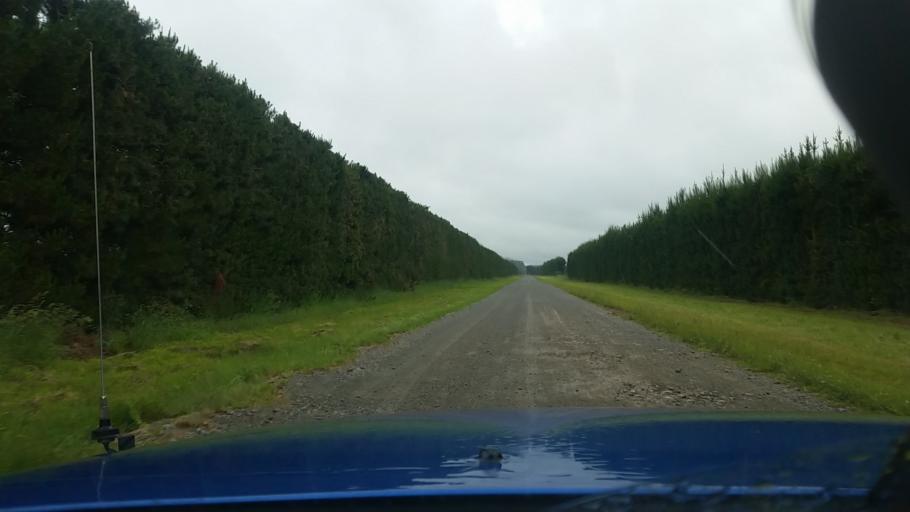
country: NZ
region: Canterbury
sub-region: Ashburton District
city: Tinwald
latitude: -43.9063
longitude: 171.5521
